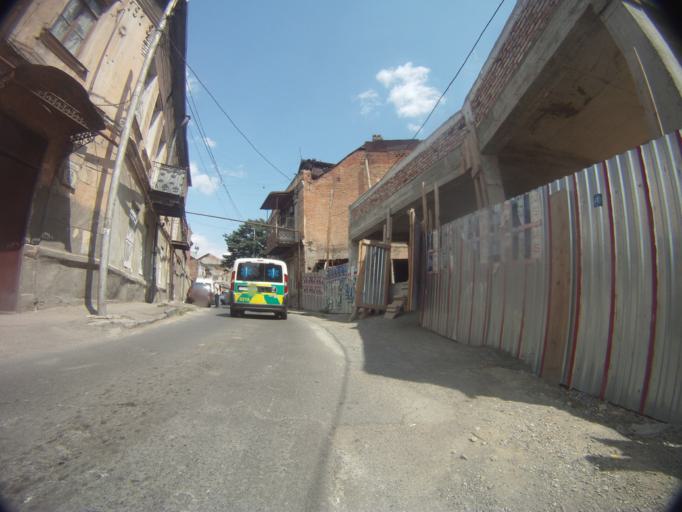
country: GE
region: T'bilisi
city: Tbilisi
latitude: 41.6900
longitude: 44.8056
